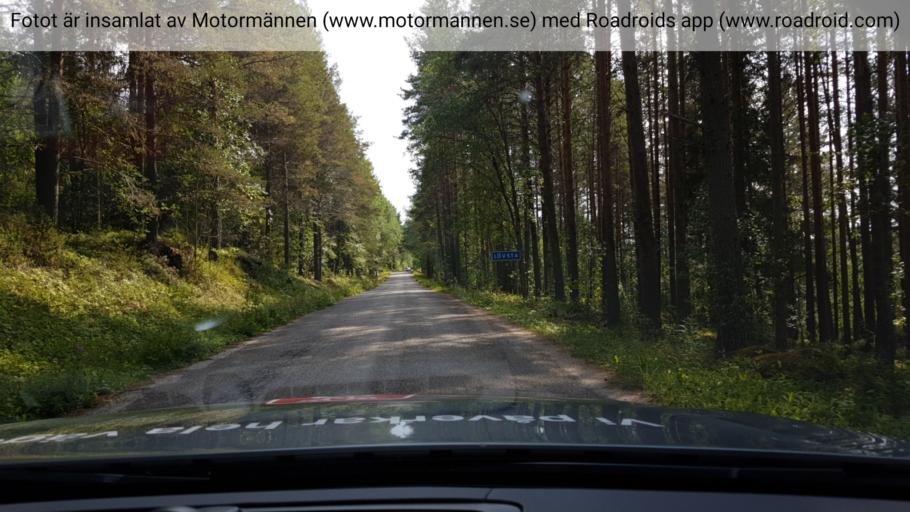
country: SE
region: Jaemtland
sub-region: OEstersunds Kommun
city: Brunflo
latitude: 63.0125
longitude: 15.1009
